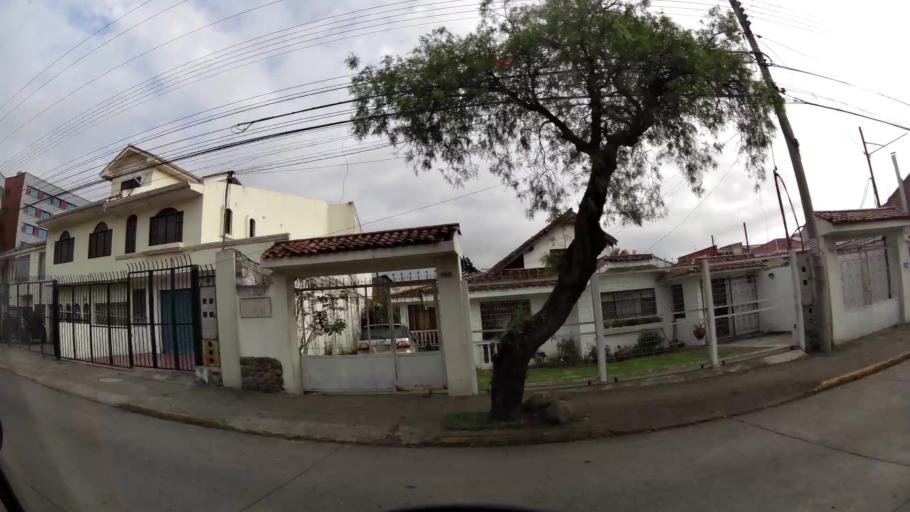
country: EC
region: Azuay
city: Cuenca
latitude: -2.9130
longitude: -79.0008
